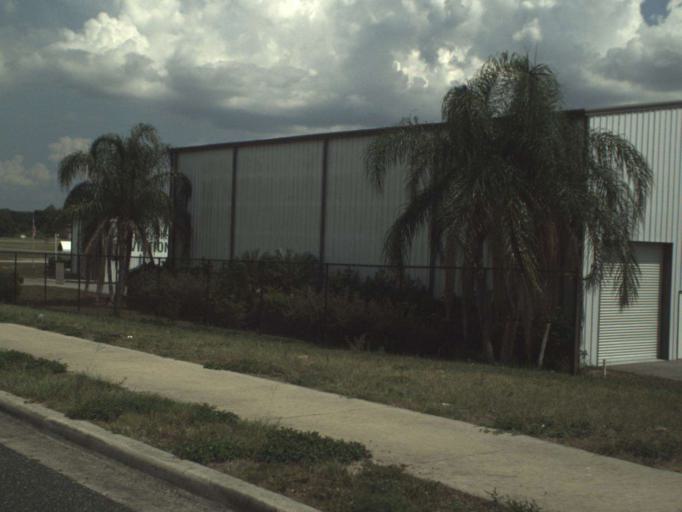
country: US
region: Florida
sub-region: Lake County
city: Silver Lake
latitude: 28.8286
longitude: -81.8059
